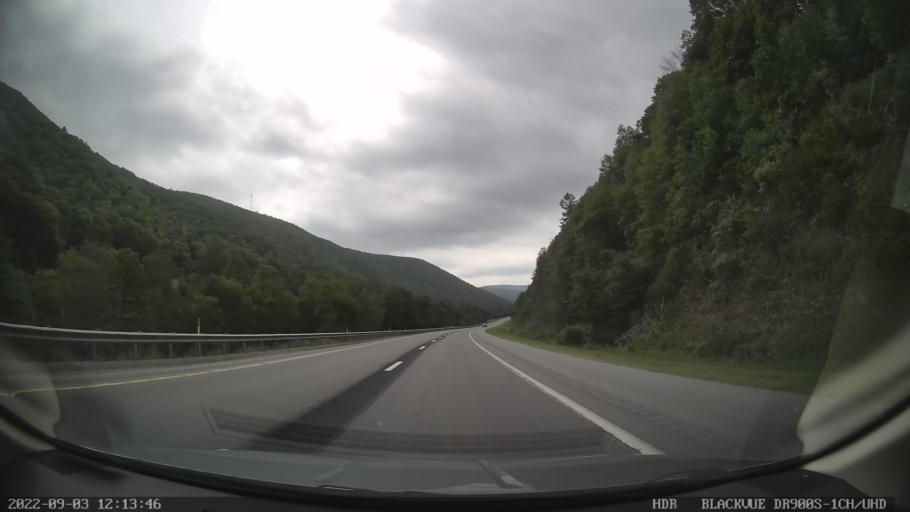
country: US
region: Pennsylvania
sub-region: Lycoming County
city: Garden View
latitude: 41.4133
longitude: -77.0685
